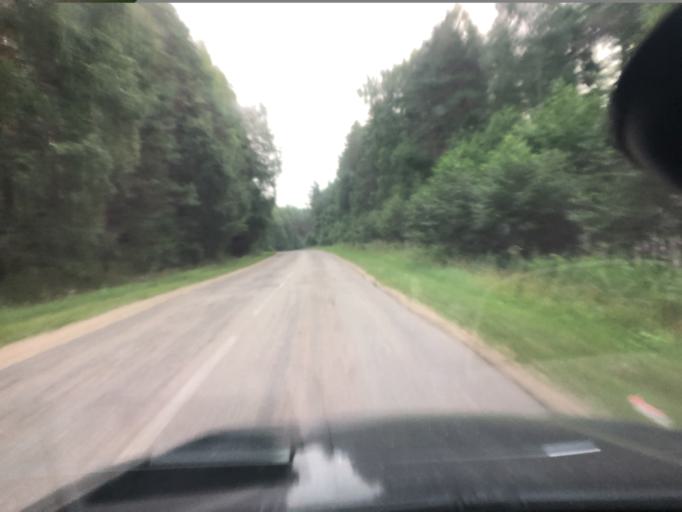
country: RU
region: Jaroslavl
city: Petrovsk
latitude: 57.0001
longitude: 39.0721
